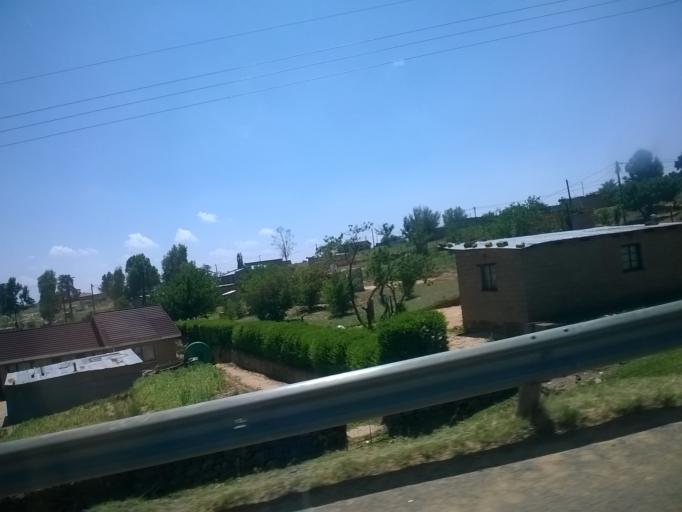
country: LS
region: Leribe
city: Maputsoe
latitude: -28.9735
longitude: 27.9776
